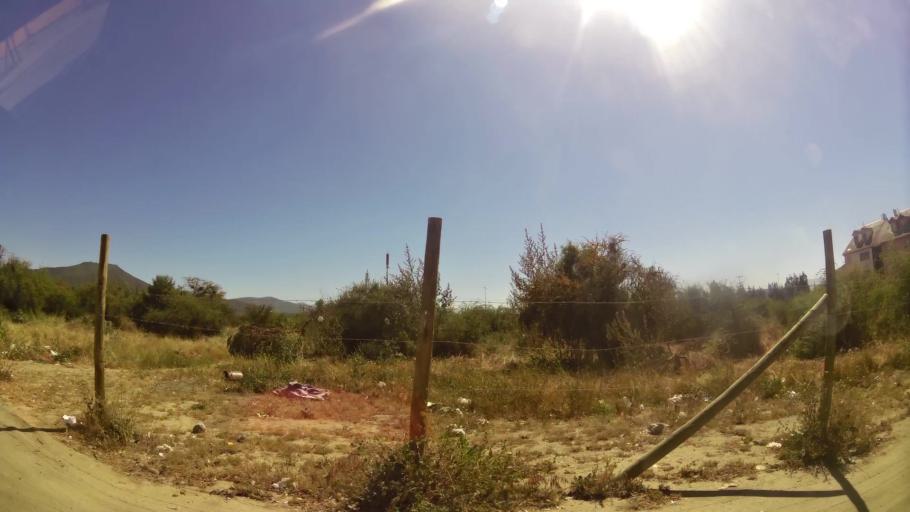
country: CL
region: Valparaiso
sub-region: Provincia de Marga Marga
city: Quilpue
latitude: -33.3045
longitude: -71.4137
